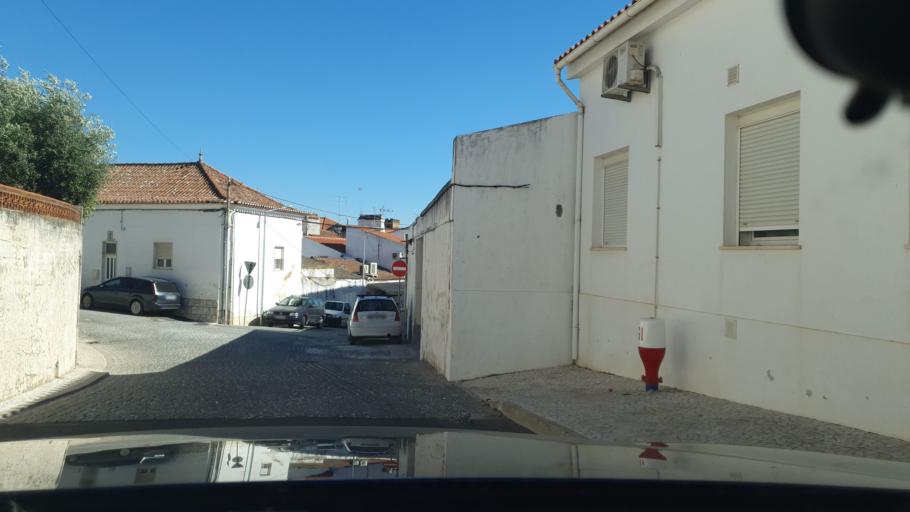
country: PT
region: Evora
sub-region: Alandroal
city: Alandroal
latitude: 38.7036
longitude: -7.4036
